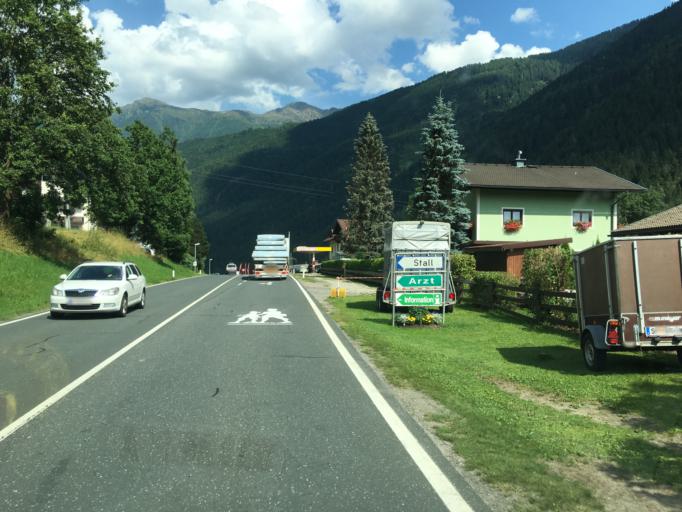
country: AT
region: Carinthia
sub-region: Politischer Bezirk Spittal an der Drau
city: Stall
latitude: 46.8856
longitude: 13.0314
